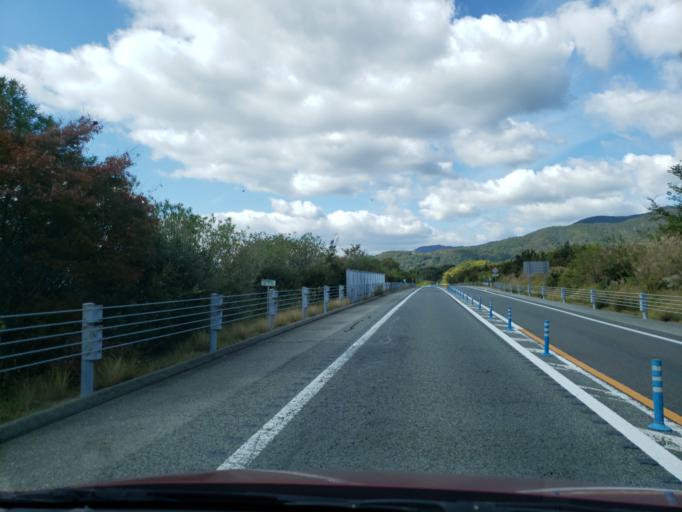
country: JP
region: Tokushima
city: Kamojimacho-jogejima
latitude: 34.1217
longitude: 134.3676
